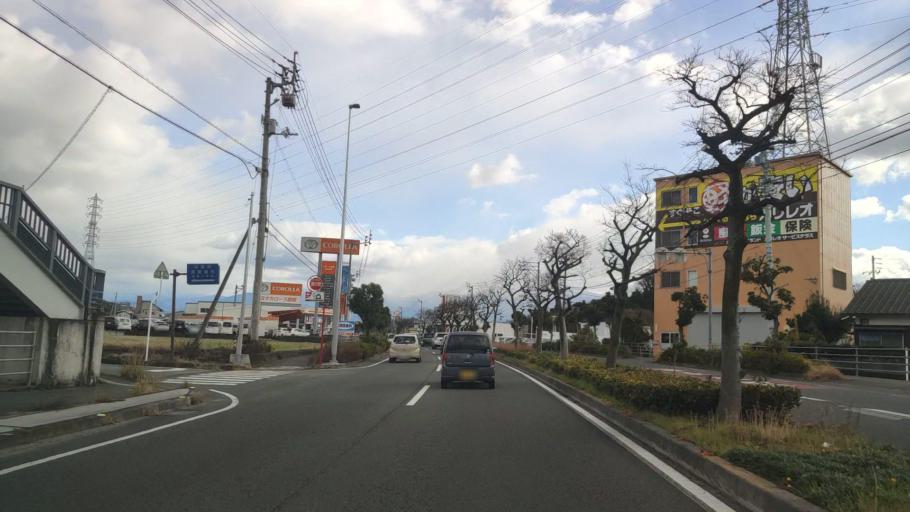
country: JP
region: Ehime
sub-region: Shikoku-chuo Shi
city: Matsuyama
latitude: 33.8209
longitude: 132.7878
